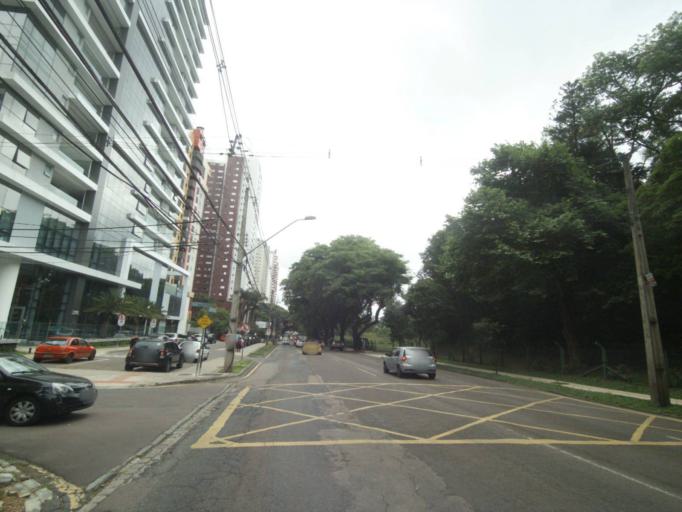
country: BR
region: Parana
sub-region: Curitiba
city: Curitiba
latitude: -25.4329
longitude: -49.3026
